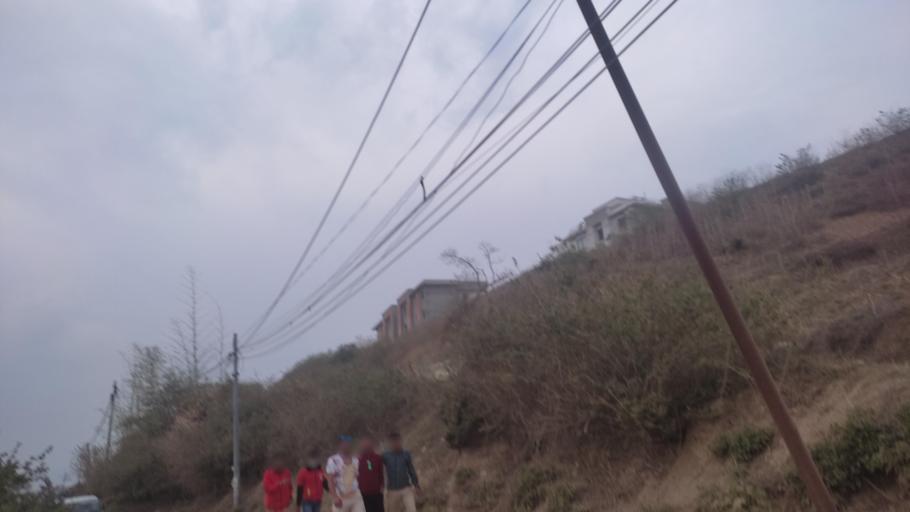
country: NP
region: Central Region
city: Kirtipur
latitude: 27.6639
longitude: 85.2875
